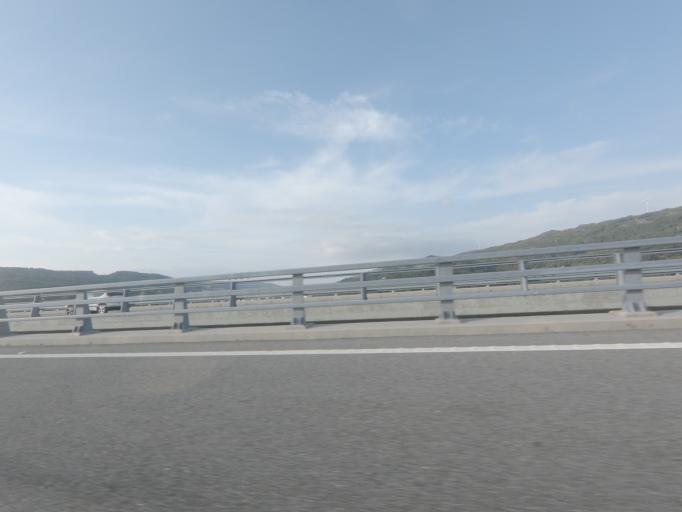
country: PT
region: Vila Real
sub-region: Vila Pouca de Aguiar
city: Vila Pouca de Aguiar
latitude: 41.4797
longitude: -7.6498
